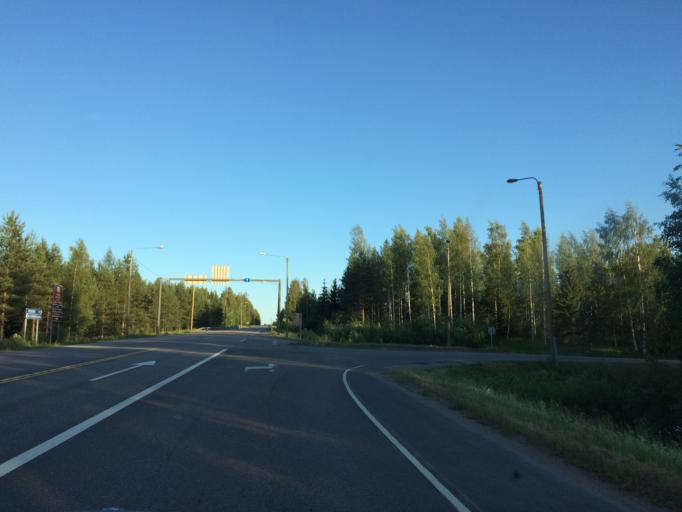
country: FI
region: Haeme
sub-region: Riihimaeki
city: Riihimaeki
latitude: 60.7515
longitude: 24.7234
